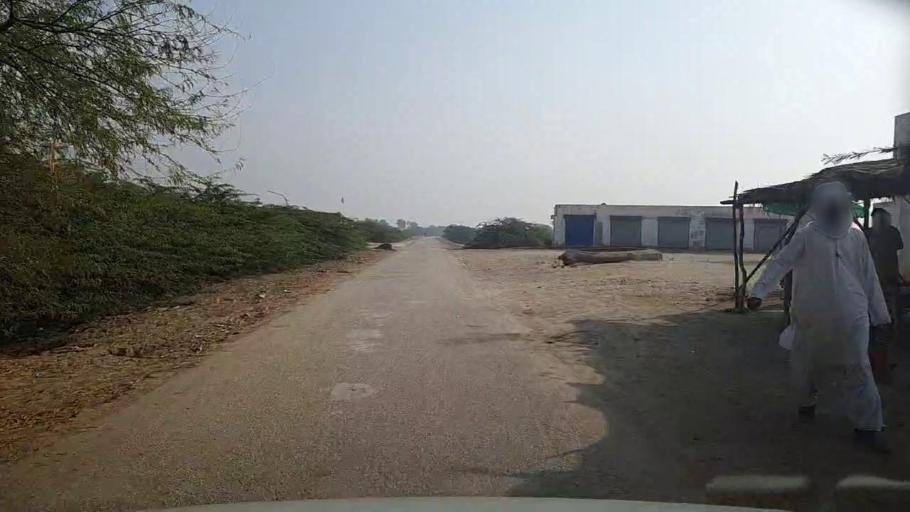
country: PK
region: Sindh
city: Kandiari
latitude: 27.0559
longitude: 68.4644
